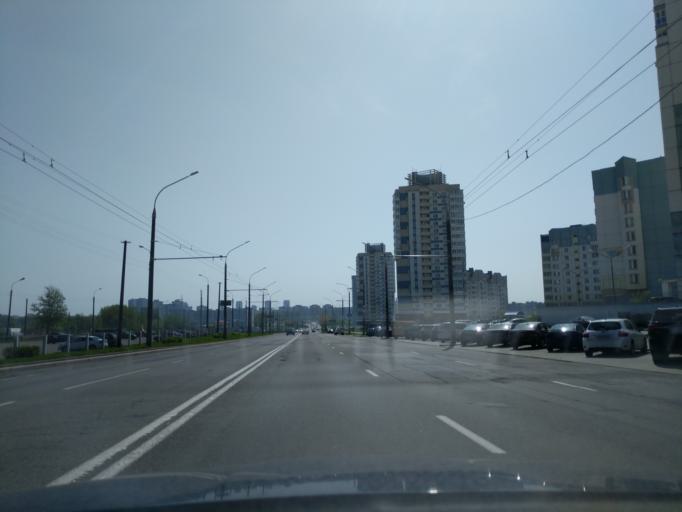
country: BY
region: Minsk
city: Novoye Medvezhino
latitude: 53.8808
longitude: 27.4545
